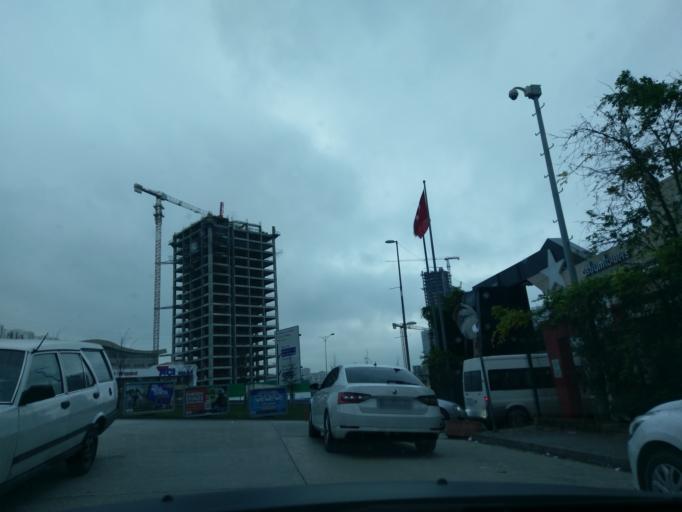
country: TR
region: Istanbul
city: Esenyurt
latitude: 41.0148
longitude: 28.6777
